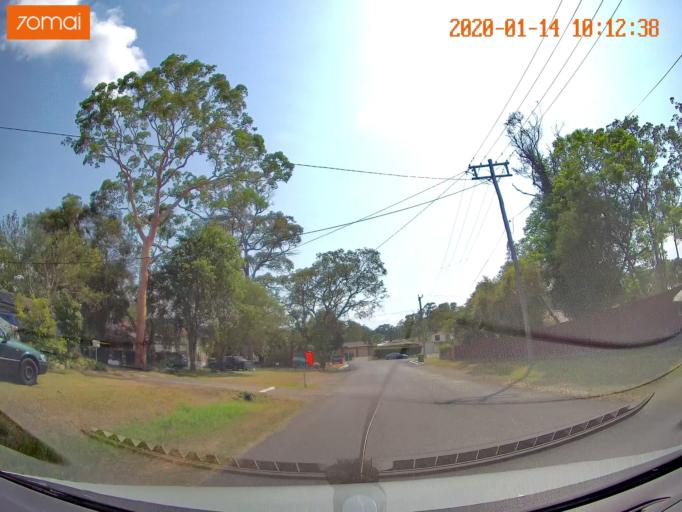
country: AU
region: New South Wales
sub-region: Lake Macquarie Shire
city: Dora Creek
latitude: -33.1151
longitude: 151.5295
